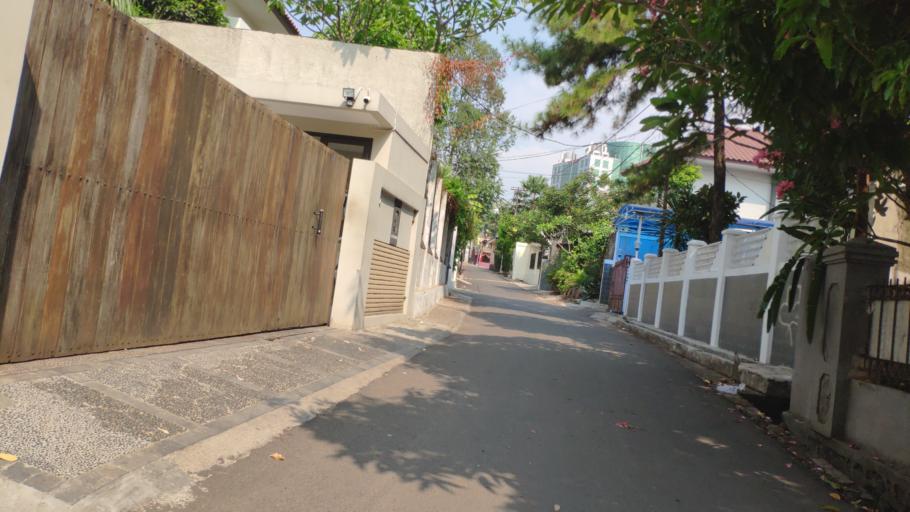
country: ID
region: Jakarta Raya
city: Jakarta
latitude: -6.2749
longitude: 106.8272
